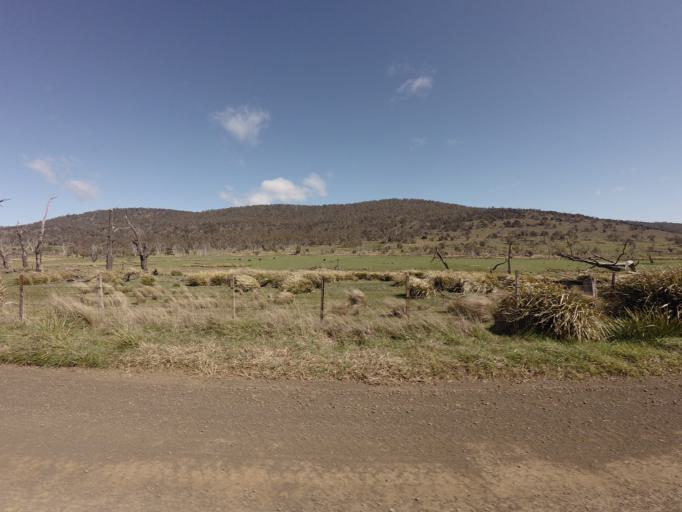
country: AU
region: Tasmania
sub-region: Northern Midlands
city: Evandale
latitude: -41.9351
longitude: 147.4190
